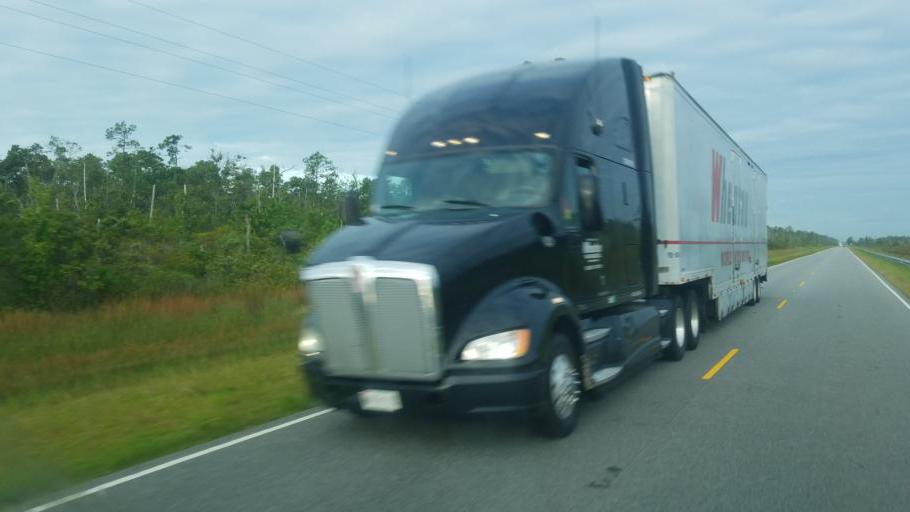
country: US
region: North Carolina
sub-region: Dare County
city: Manteo
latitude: 35.8704
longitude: -75.7937
